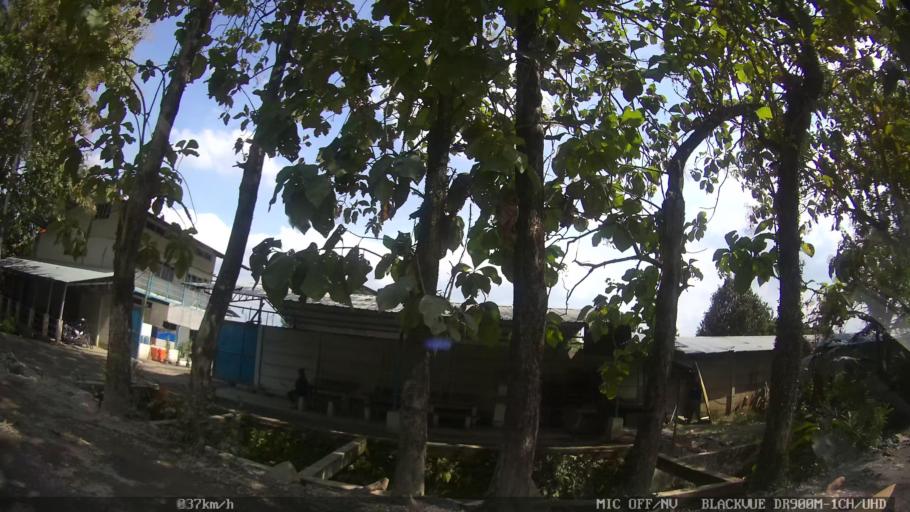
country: ID
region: North Sumatra
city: Binjai
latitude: 3.6347
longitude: 98.5300
